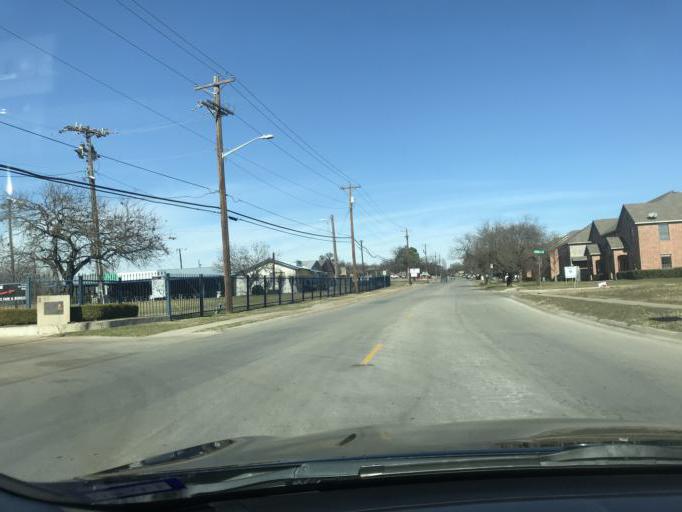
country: US
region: Texas
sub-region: Denton County
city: Denton
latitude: 33.2331
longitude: -97.1370
